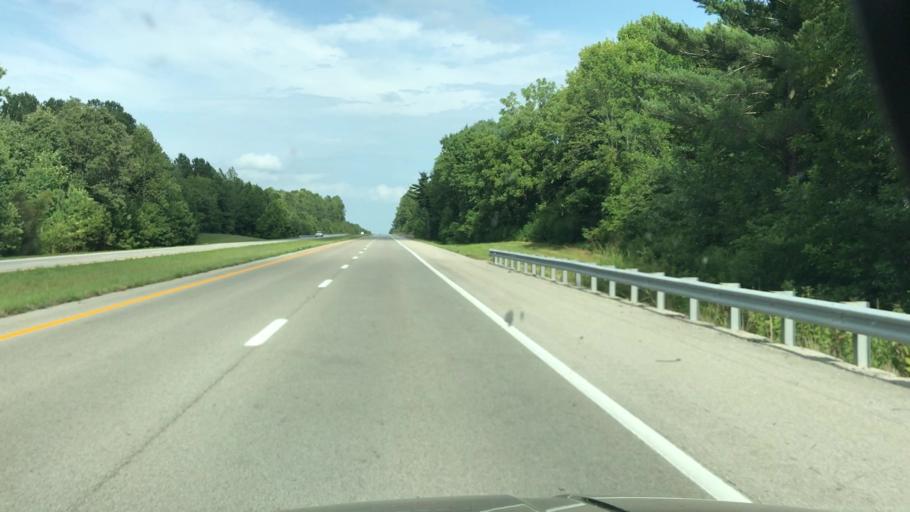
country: US
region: Kentucky
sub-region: Hopkins County
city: Nortonville
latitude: 37.2043
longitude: -87.5134
